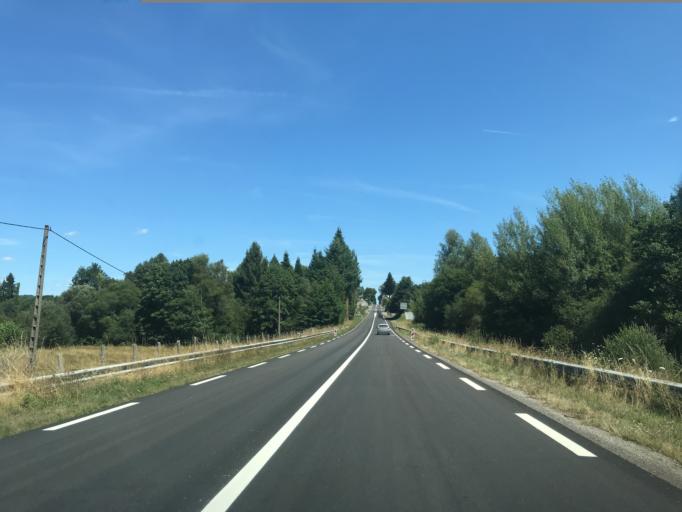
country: FR
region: Limousin
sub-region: Departement de la Correze
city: Egletons
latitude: 45.3732
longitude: 2.0043
